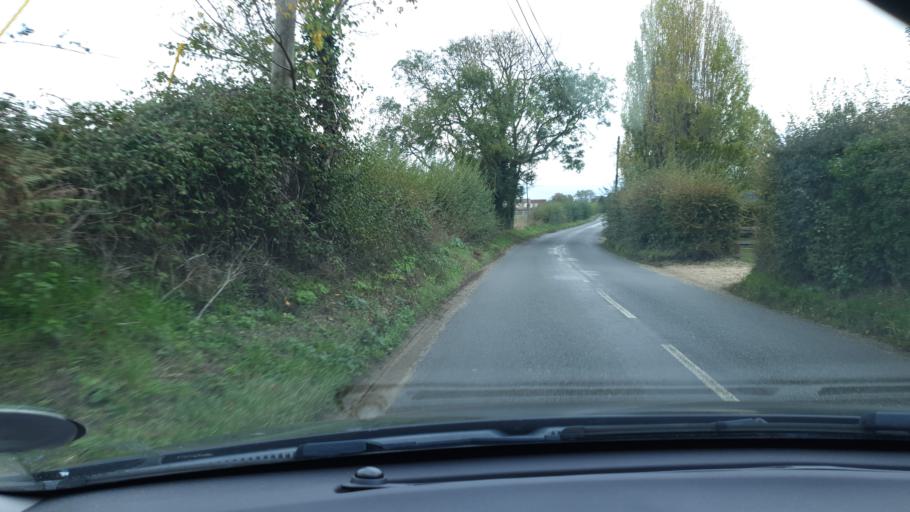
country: GB
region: England
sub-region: Essex
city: Mistley
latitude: 51.9378
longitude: 1.0949
